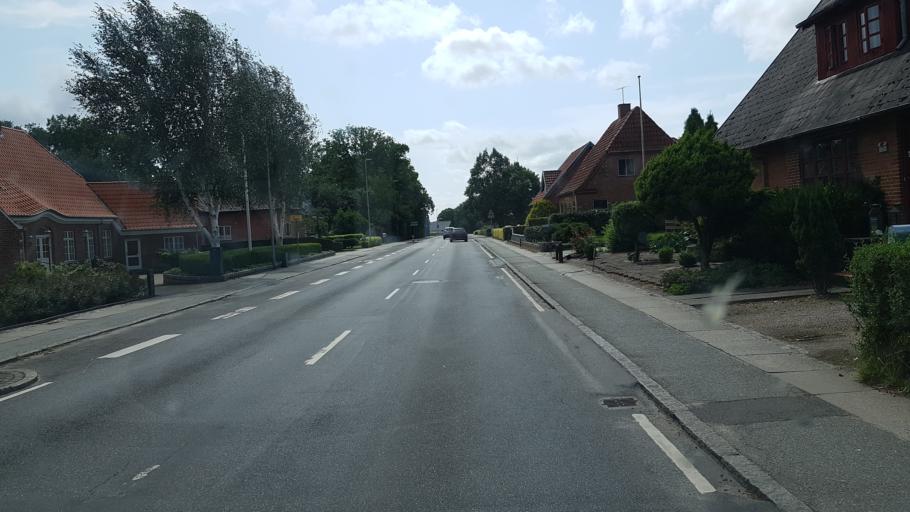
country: DK
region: South Denmark
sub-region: Vejen Kommune
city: Vejen
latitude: 55.5688
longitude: 9.1366
